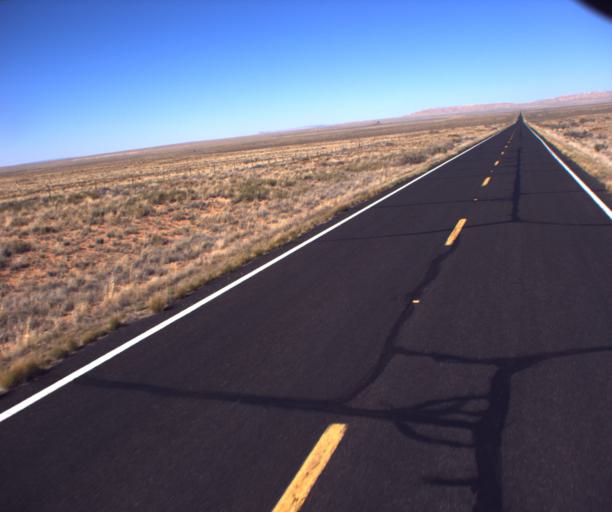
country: US
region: Arizona
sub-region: Navajo County
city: First Mesa
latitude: 35.6714
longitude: -110.4969
